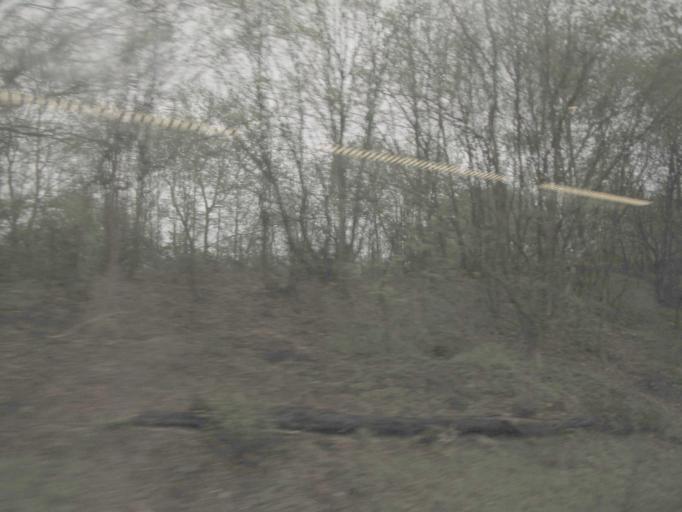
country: GB
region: England
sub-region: Surrey
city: Frimley
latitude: 51.3226
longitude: -0.7680
